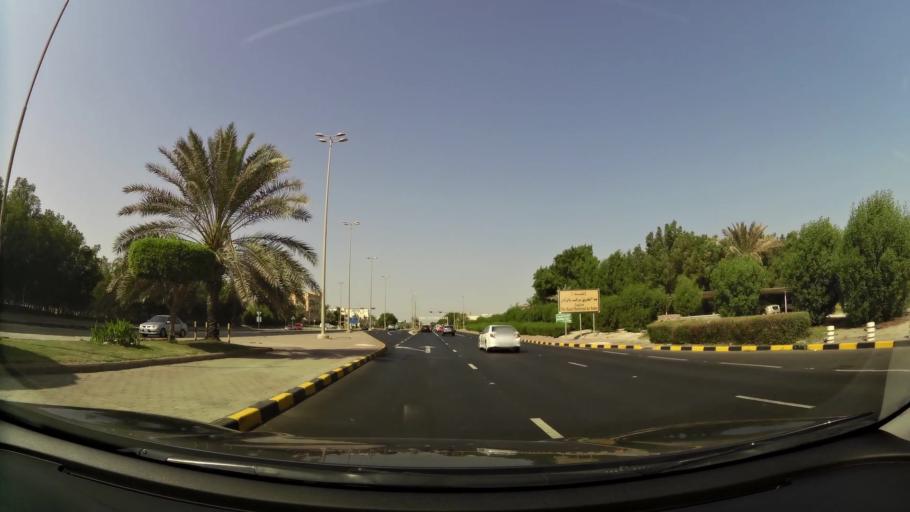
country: KW
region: Muhafazat Hawalli
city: Salwa
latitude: 29.2788
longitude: 48.0882
